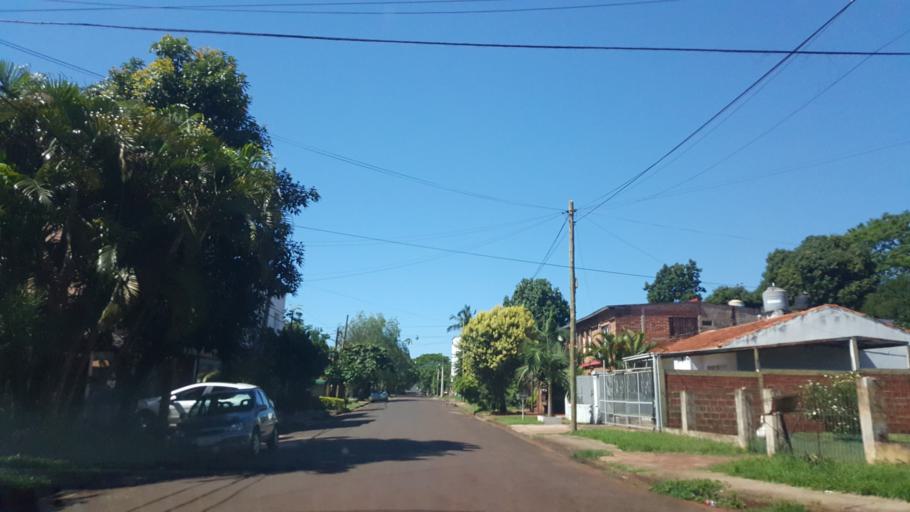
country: AR
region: Misiones
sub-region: Departamento de Capital
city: Posadas
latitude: -27.3814
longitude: -55.9020
